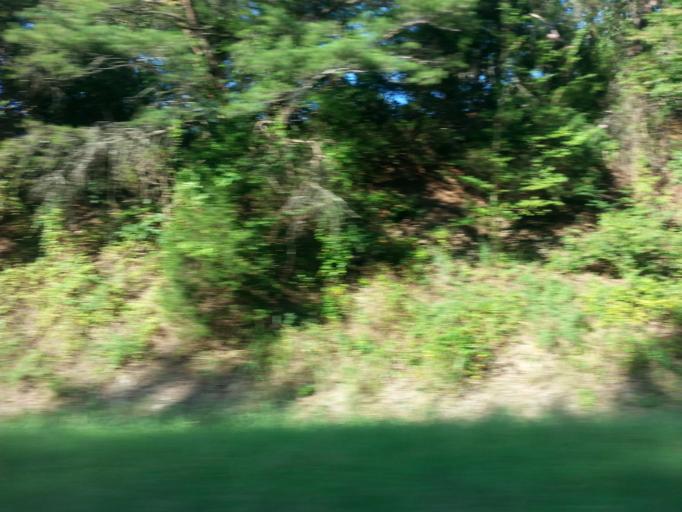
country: US
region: Alabama
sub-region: Colbert County
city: Tuscumbia
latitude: 34.7139
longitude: -87.7796
